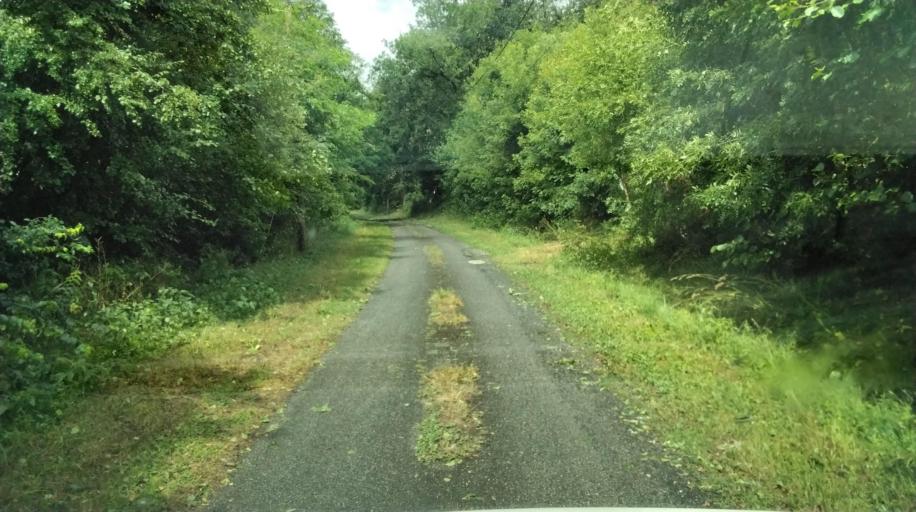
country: FR
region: Midi-Pyrenees
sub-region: Departement de la Haute-Garonne
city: Rieumes
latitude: 43.4226
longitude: 1.1589
